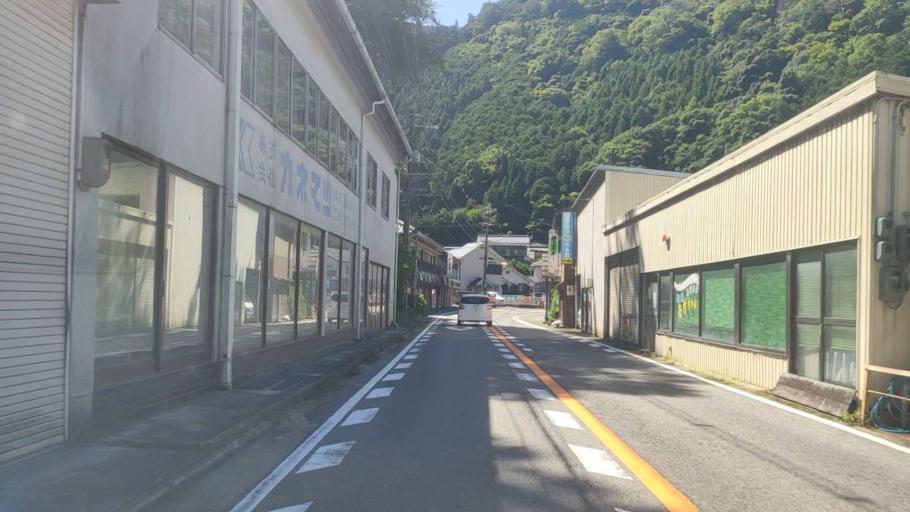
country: JP
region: Nara
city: Yoshino-cho
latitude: 34.3557
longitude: 135.9241
